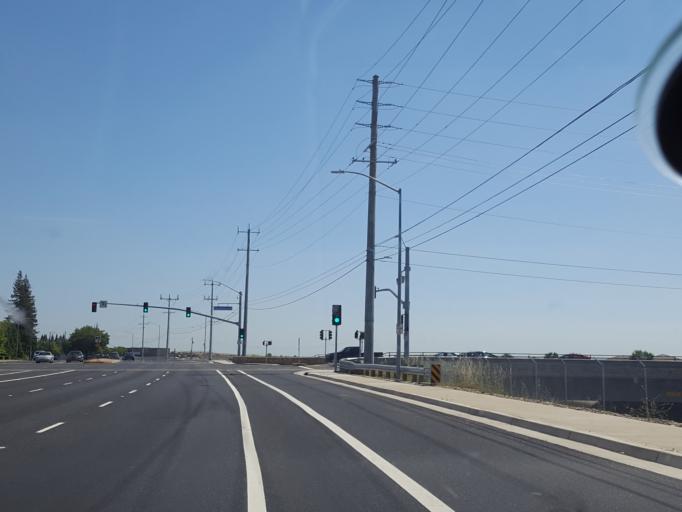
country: US
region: California
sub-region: Sacramento County
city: Rancho Cordova
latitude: 38.5853
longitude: -121.2655
